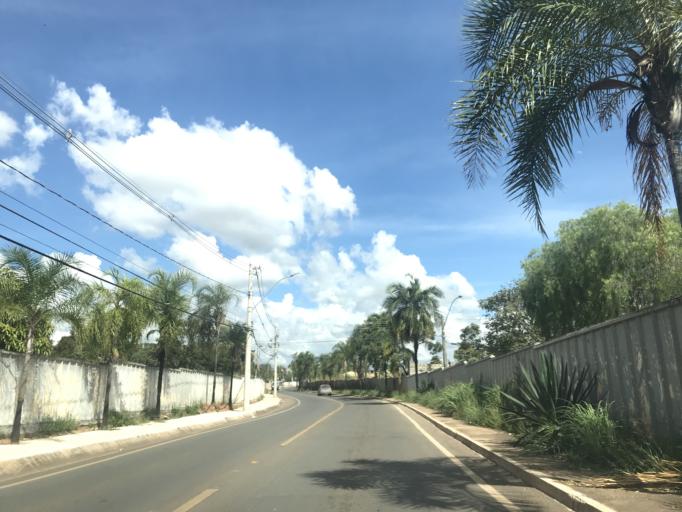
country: BR
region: Federal District
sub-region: Brasilia
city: Brasilia
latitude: -15.8672
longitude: -47.7944
